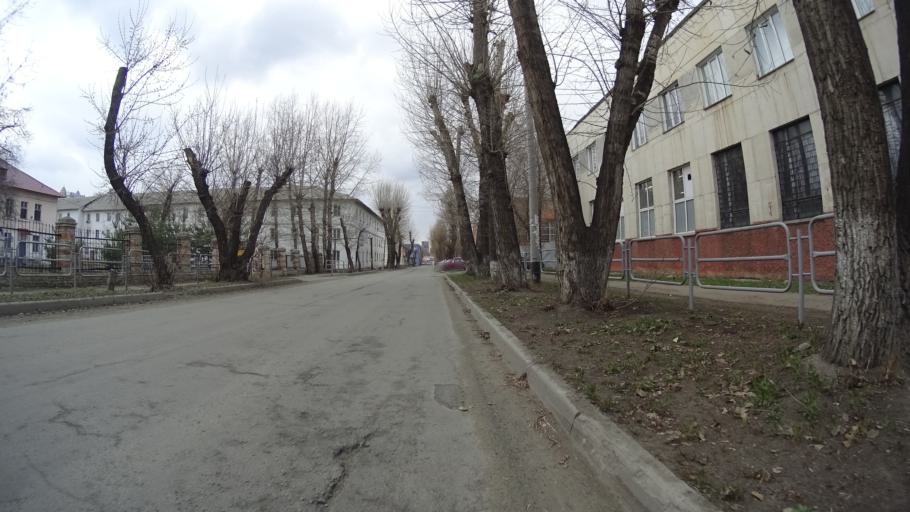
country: RU
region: Chelyabinsk
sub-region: Gorod Chelyabinsk
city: Chelyabinsk
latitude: 55.1657
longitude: 61.4378
